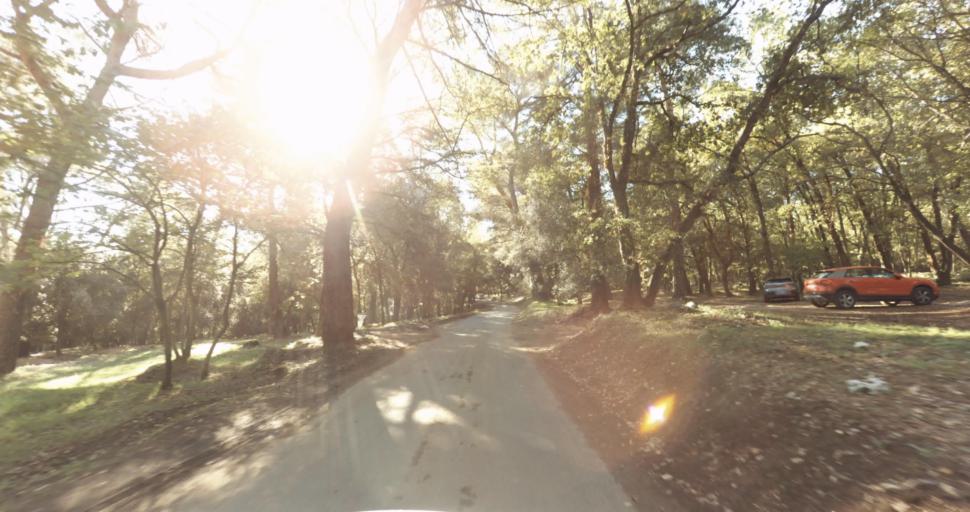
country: FR
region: Provence-Alpes-Cote d'Azur
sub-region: Departement des Alpes-Maritimes
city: Vence
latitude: 43.7101
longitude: 7.0954
